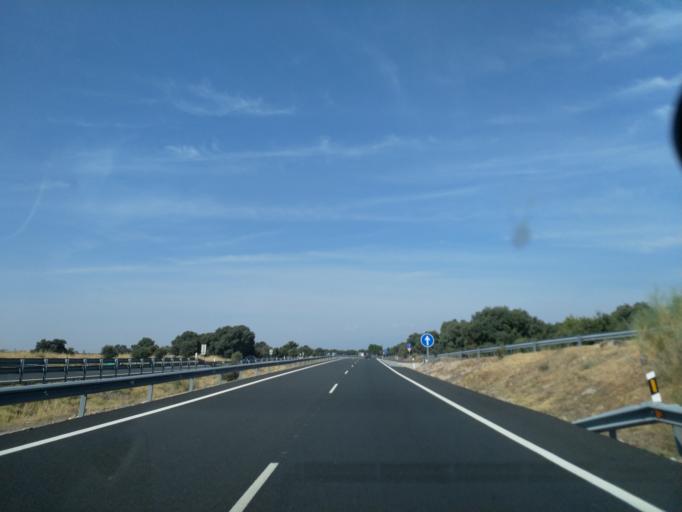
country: ES
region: Castille-La Mancha
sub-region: Province of Toledo
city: Alcanizo
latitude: 39.9197
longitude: -5.0823
